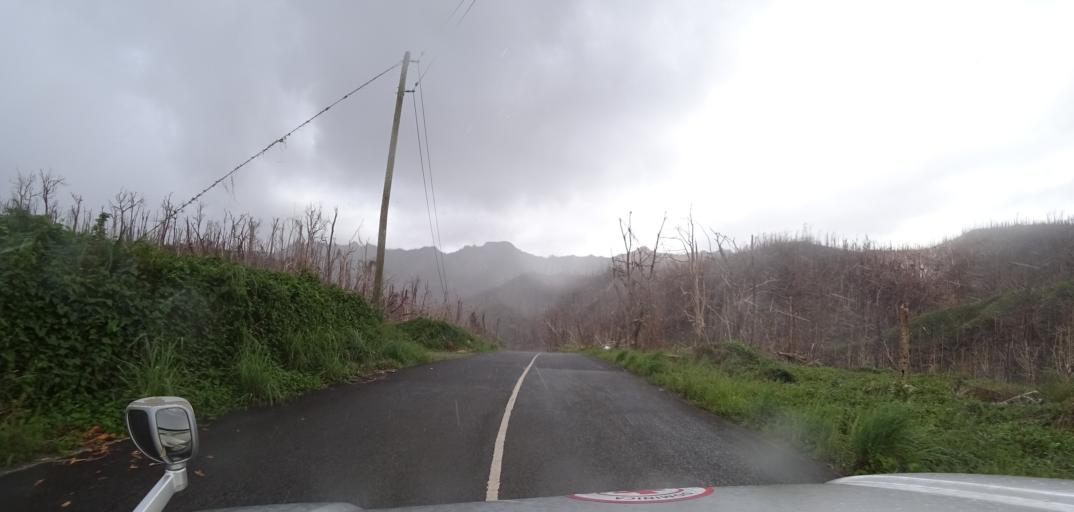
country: DM
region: Saint David
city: Castle Bruce
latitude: 15.4753
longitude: -61.2942
